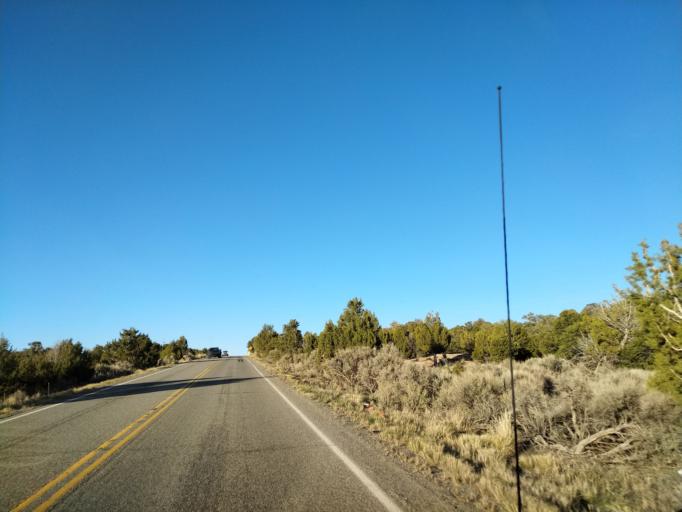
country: US
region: Colorado
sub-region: Mesa County
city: Redlands
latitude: 38.9967
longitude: -108.7150
